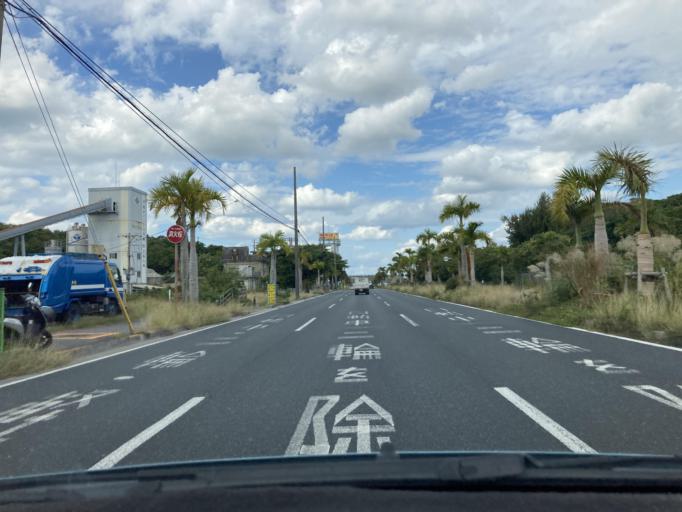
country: JP
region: Okinawa
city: Chatan
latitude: 26.3336
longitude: 127.7515
